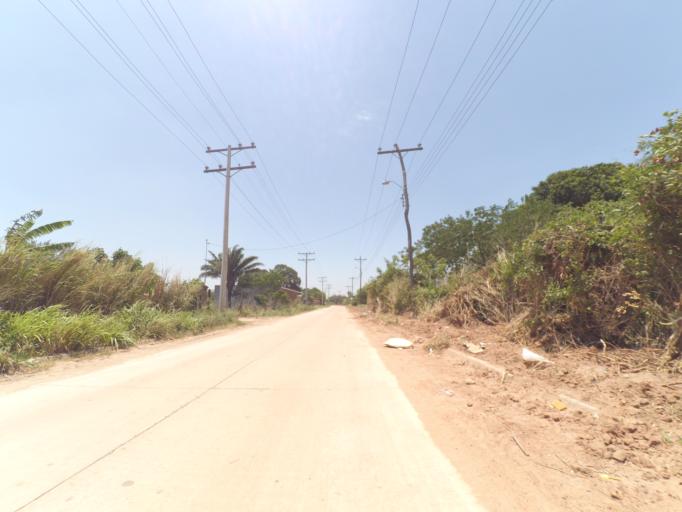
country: BO
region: Santa Cruz
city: Santa Cruz de la Sierra
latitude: -17.8620
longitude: -63.2314
